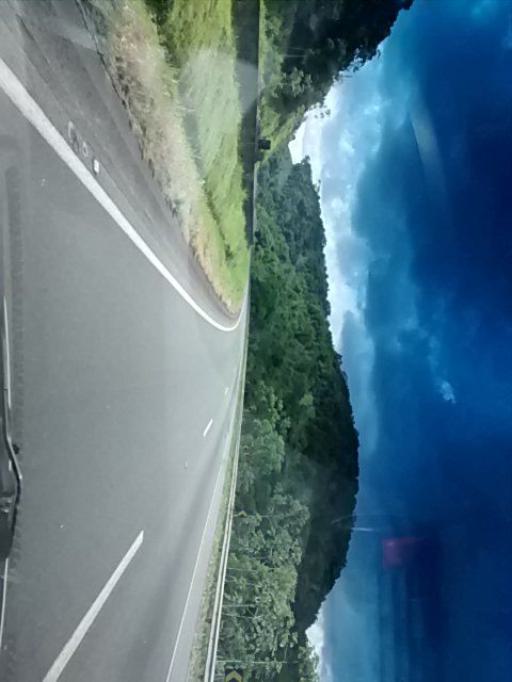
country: BR
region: Sao Paulo
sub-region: Miracatu
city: Miracatu
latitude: -24.2318
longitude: -47.3603
